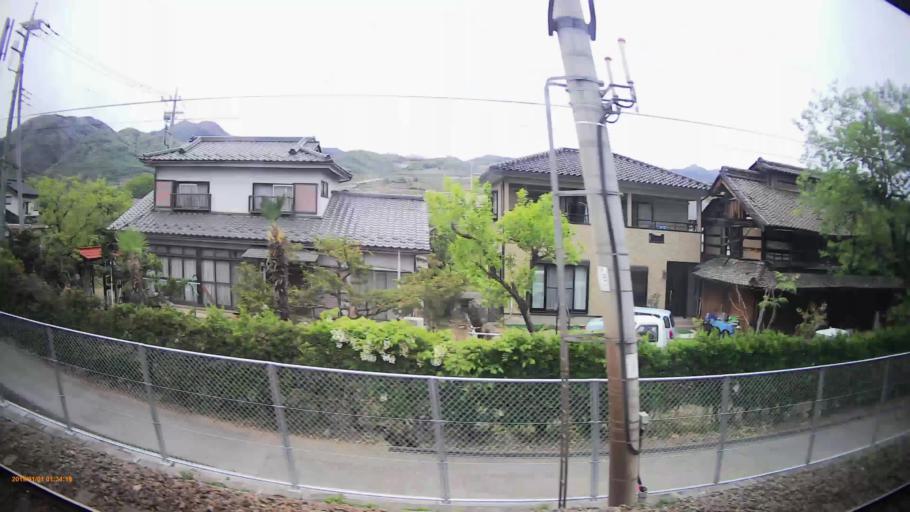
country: JP
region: Yamanashi
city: Isawa
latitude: 35.6856
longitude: 138.6742
